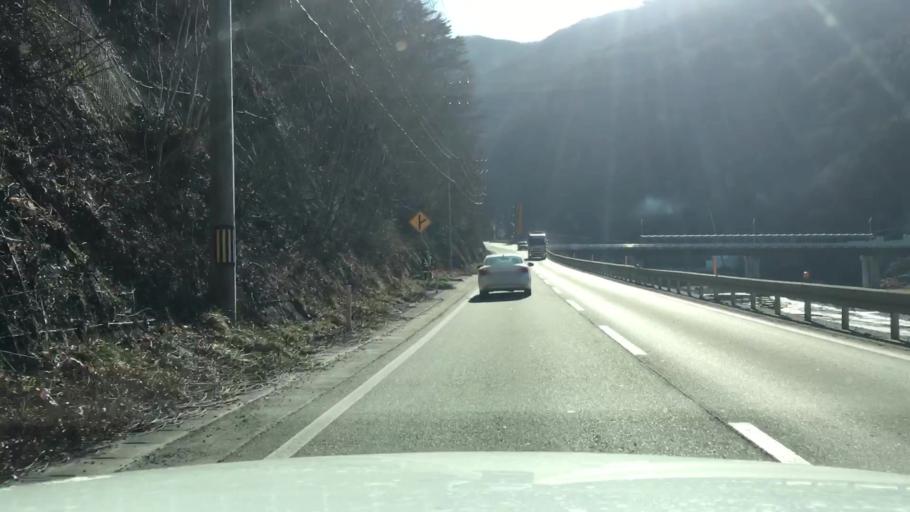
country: JP
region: Iwate
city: Miyako
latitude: 39.6176
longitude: 141.7952
